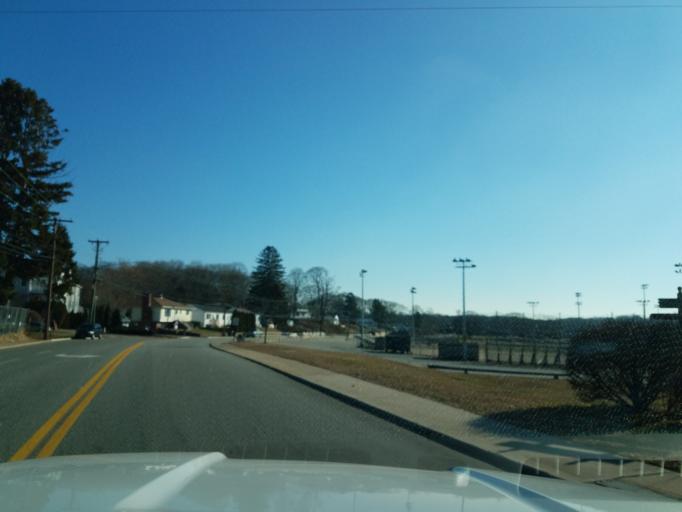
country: US
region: Connecticut
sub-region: New London County
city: Groton
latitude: 41.3573
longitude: -72.0763
